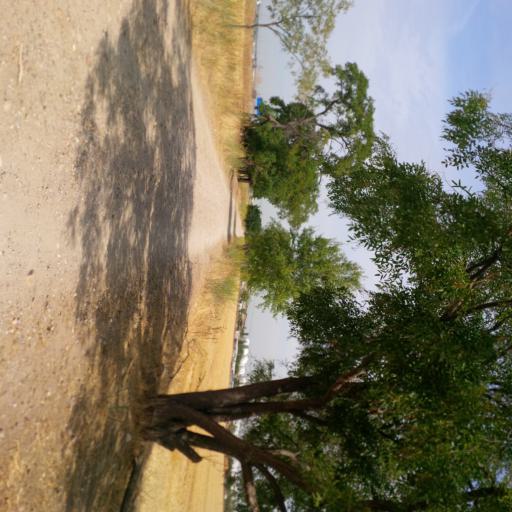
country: ES
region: Madrid
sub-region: Provincia de Madrid
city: Mejorada del Campo
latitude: 40.4157
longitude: -3.4984
